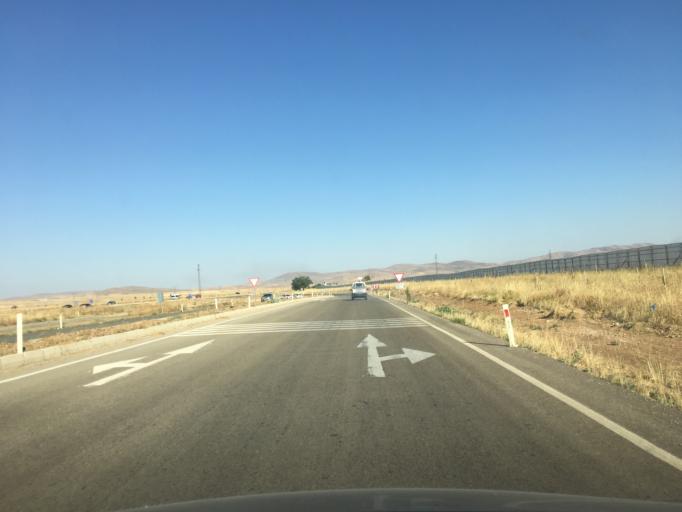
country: TR
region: Kirsehir
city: Akpinar
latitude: 39.3281
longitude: 34.0365
